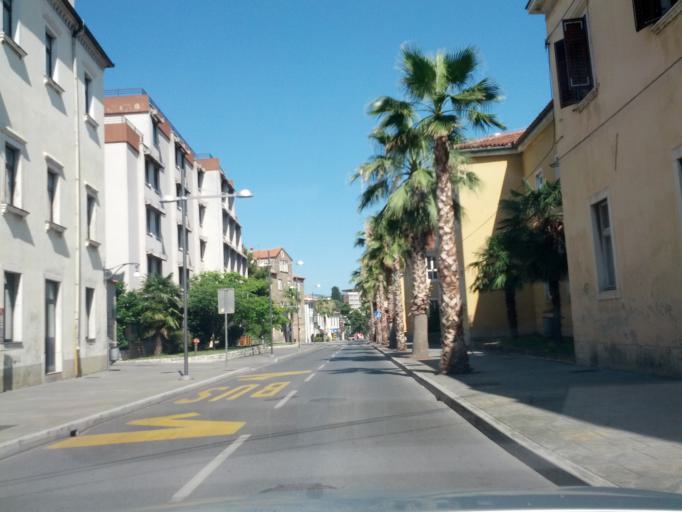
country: SI
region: Koper-Capodistria
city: Koper
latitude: 45.5484
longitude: 13.7314
